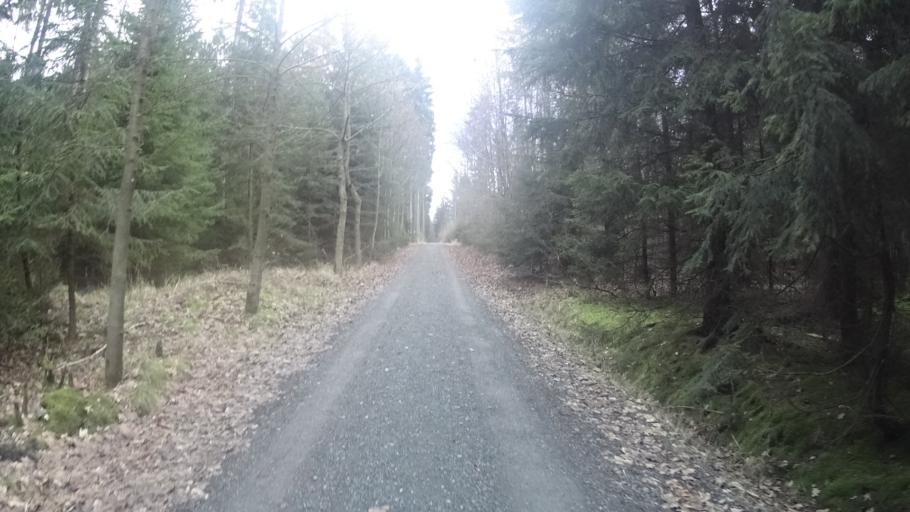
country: DE
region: Thuringia
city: Langenwolschendorf
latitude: 50.6140
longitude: 11.9881
